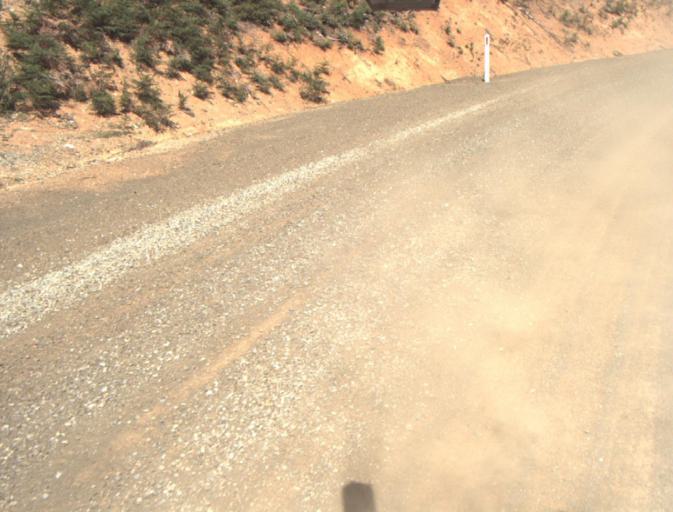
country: AU
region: Tasmania
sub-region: Launceston
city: Newstead
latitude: -41.2956
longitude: 147.3399
